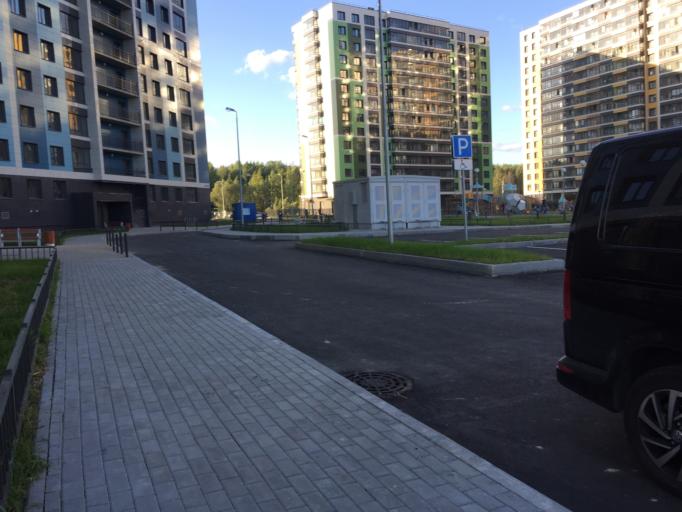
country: RU
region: Leningrad
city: Murino
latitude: 60.0686
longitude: 30.4471
